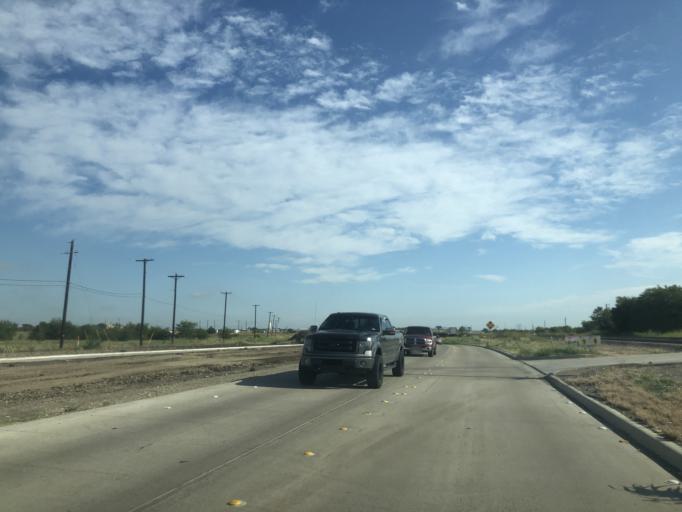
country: US
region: Texas
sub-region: Denton County
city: Justin
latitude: 33.0488
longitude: -97.3025
